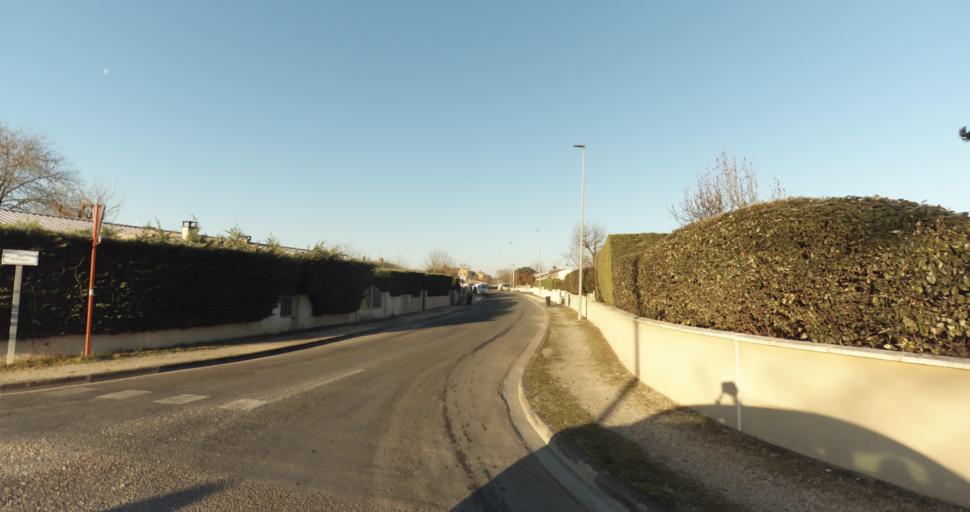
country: FR
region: Aquitaine
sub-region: Departement de la Gironde
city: Carbon-Blanc
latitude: 44.9024
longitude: -0.4995
